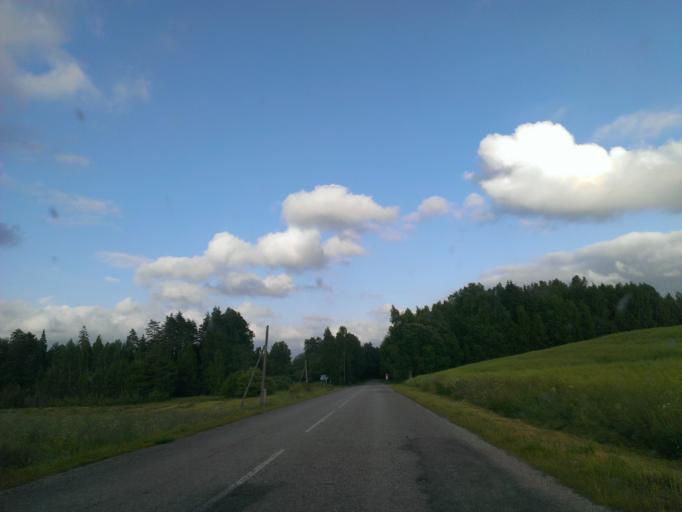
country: LV
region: Skrunda
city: Skrunda
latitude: 56.6900
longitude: 21.8751
